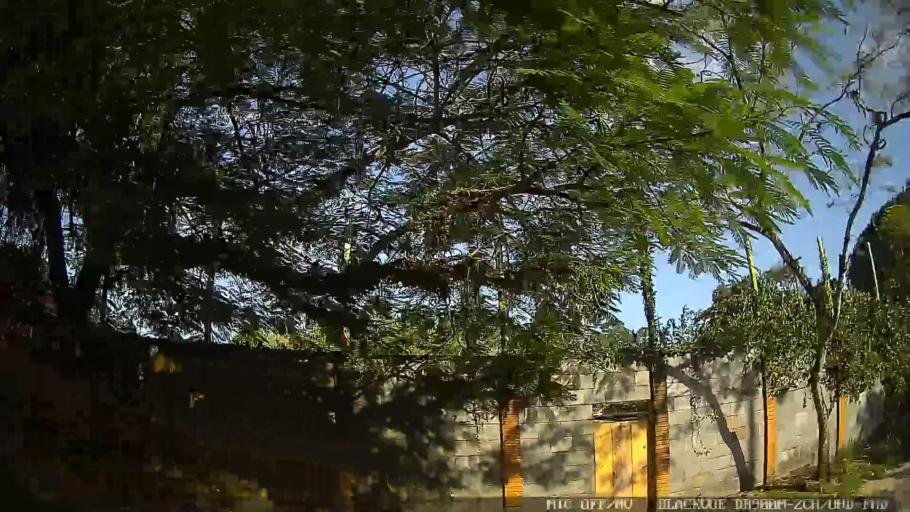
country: BR
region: Sao Paulo
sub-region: Itanhaem
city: Itanhaem
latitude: -24.1733
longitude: -46.8234
